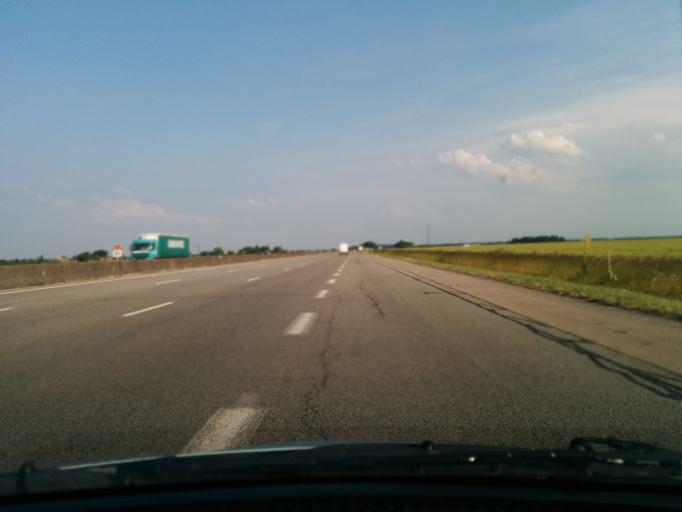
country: FR
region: Haute-Normandie
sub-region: Departement de l'Eure
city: Saint-Aubin-sur-Gaillon
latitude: 49.1318
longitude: 1.3175
